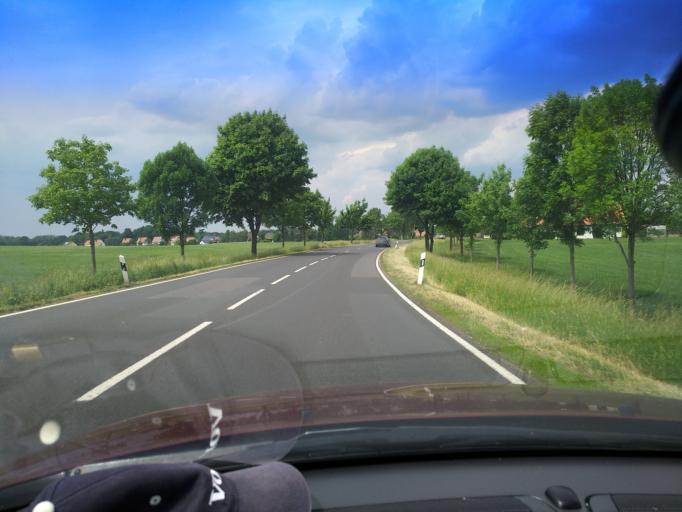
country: DE
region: Saxony
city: Quitzdorf
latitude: 51.2935
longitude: 14.7812
